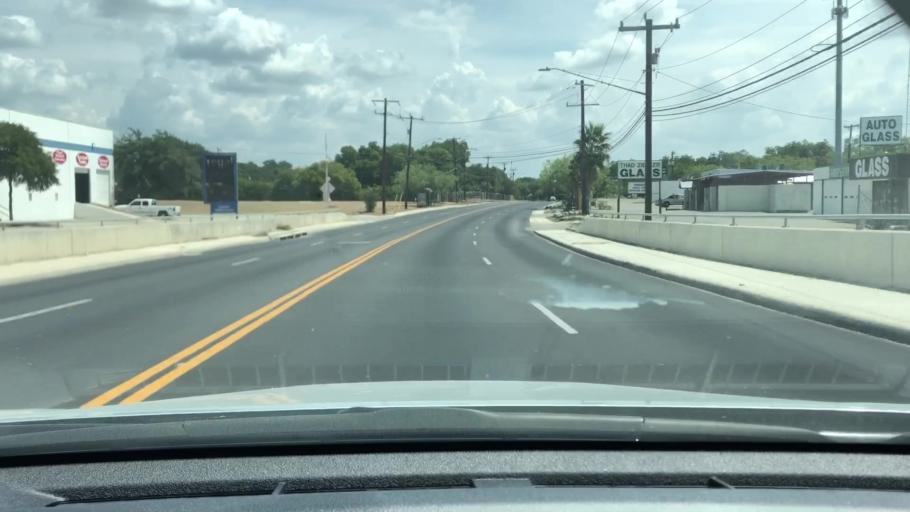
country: US
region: Texas
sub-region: Bexar County
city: Kirby
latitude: 29.4849
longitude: -98.4149
